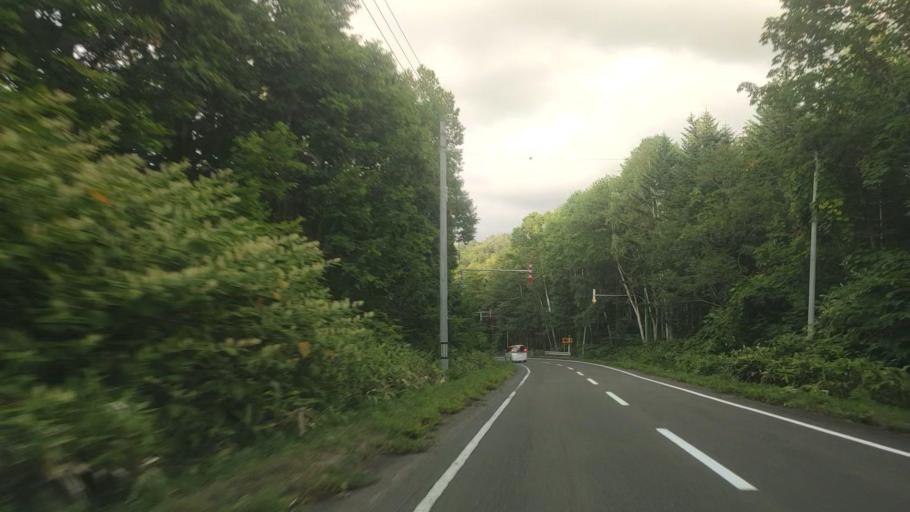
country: JP
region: Hokkaido
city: Bibai
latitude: 43.1755
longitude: 142.0690
